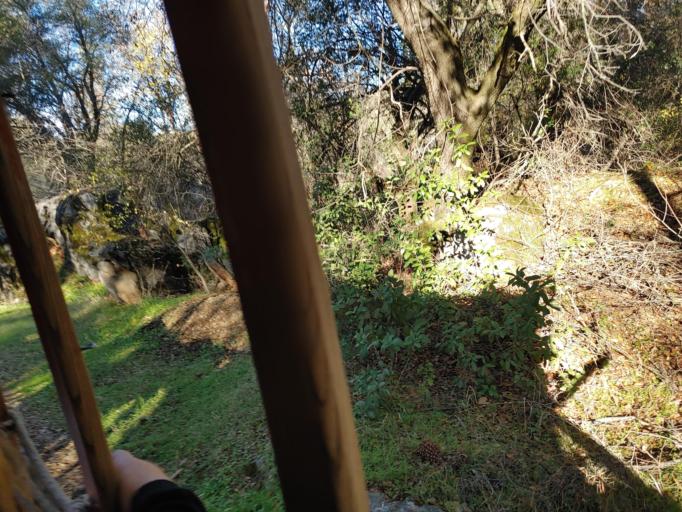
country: US
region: California
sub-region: Tuolumne County
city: Columbia
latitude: 38.0334
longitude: -120.3973
